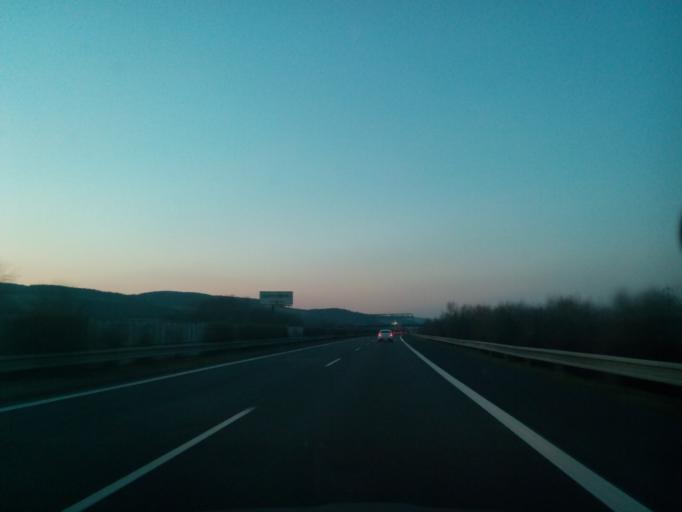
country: SK
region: Presovsky
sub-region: Okres Presov
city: Presov
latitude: 48.8741
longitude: 21.2537
